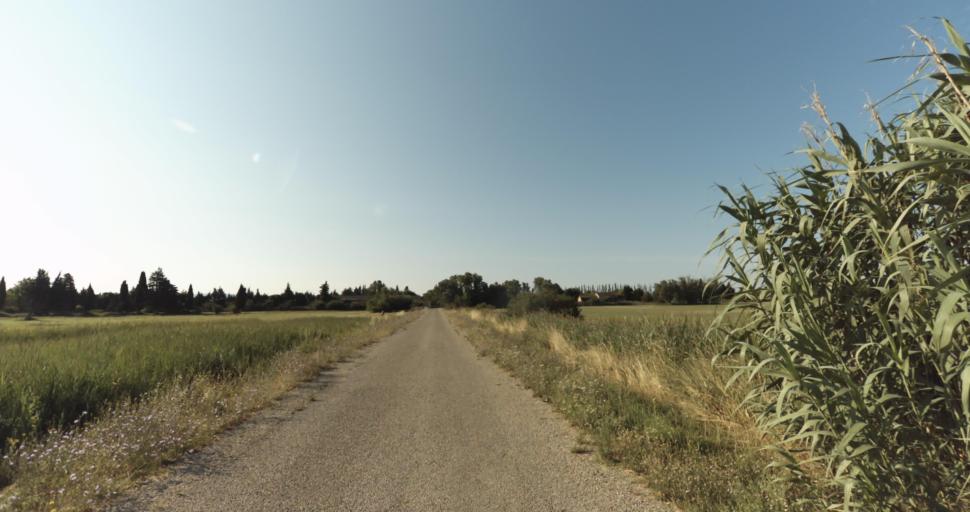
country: FR
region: Provence-Alpes-Cote d'Azur
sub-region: Departement du Vaucluse
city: Sarrians
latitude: 44.0538
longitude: 4.9590
